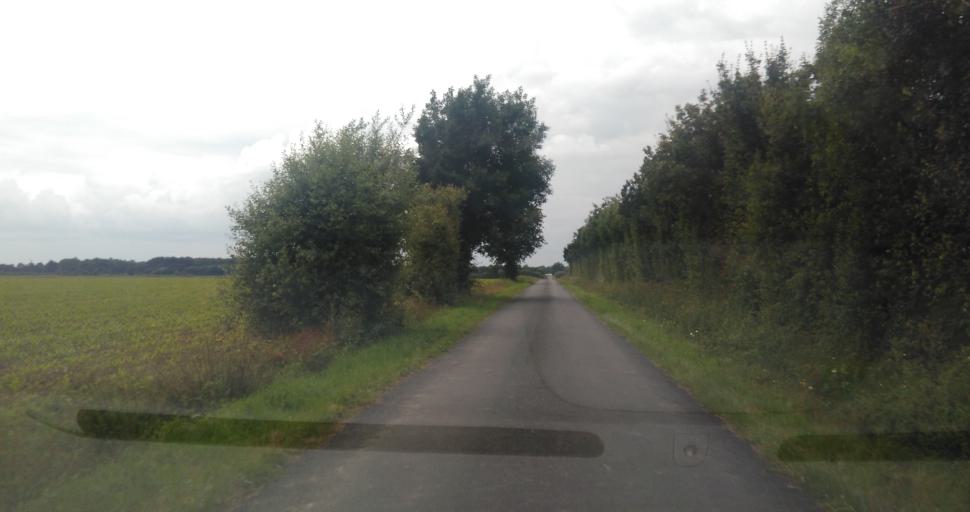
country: FR
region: Pays de la Loire
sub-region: Departement de la Vendee
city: Saint-Georges-de-Montaigu
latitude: 46.9261
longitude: -1.3175
